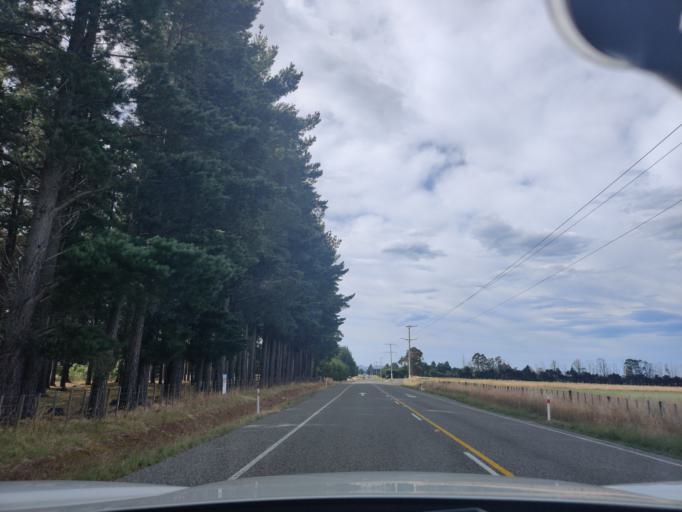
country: NZ
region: Wellington
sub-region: Masterton District
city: Masterton
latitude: -40.8442
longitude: 175.6324
